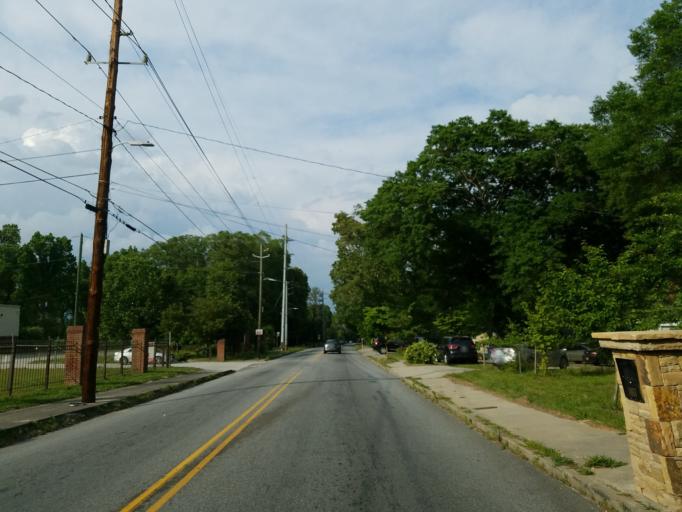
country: US
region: Georgia
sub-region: Cobb County
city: Vinings
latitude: 33.7949
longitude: -84.4916
